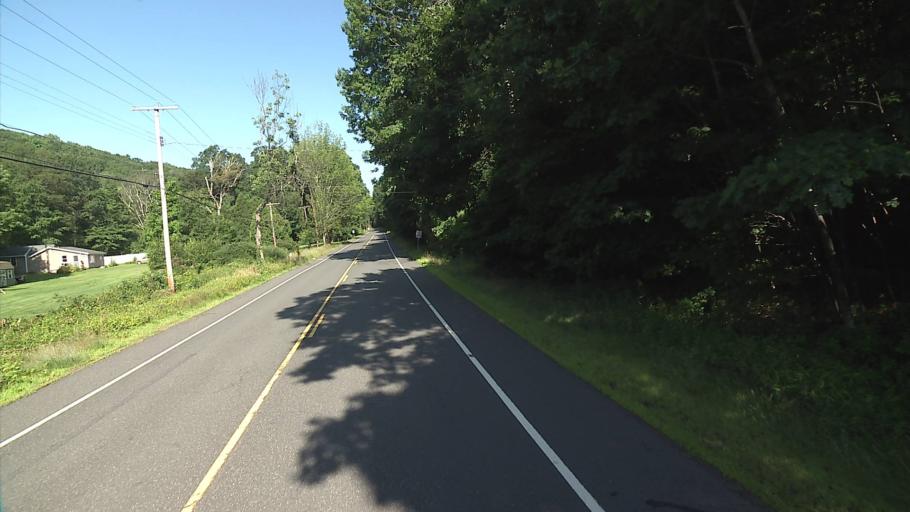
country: US
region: Connecticut
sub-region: Hartford County
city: North Granby
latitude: 41.9731
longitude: -72.8729
